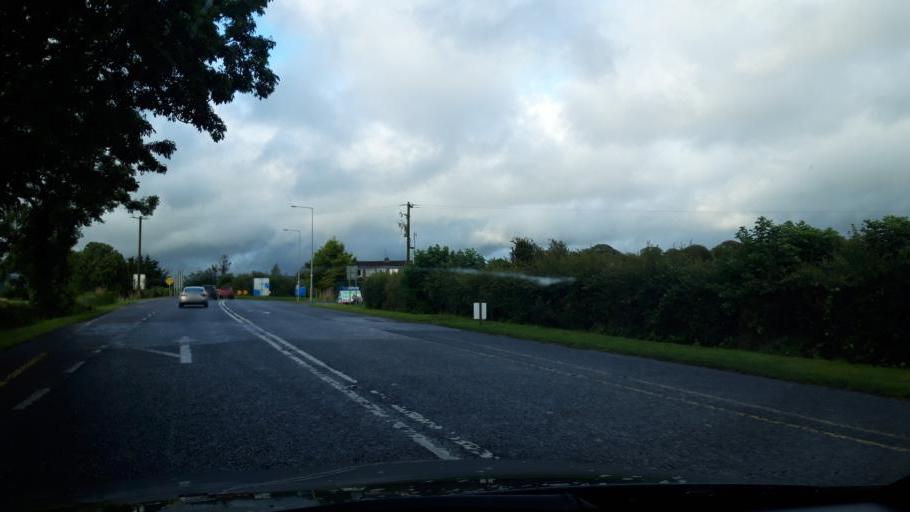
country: IE
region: Munster
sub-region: County Cork
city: Fermoy
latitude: 52.1608
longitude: -8.2698
